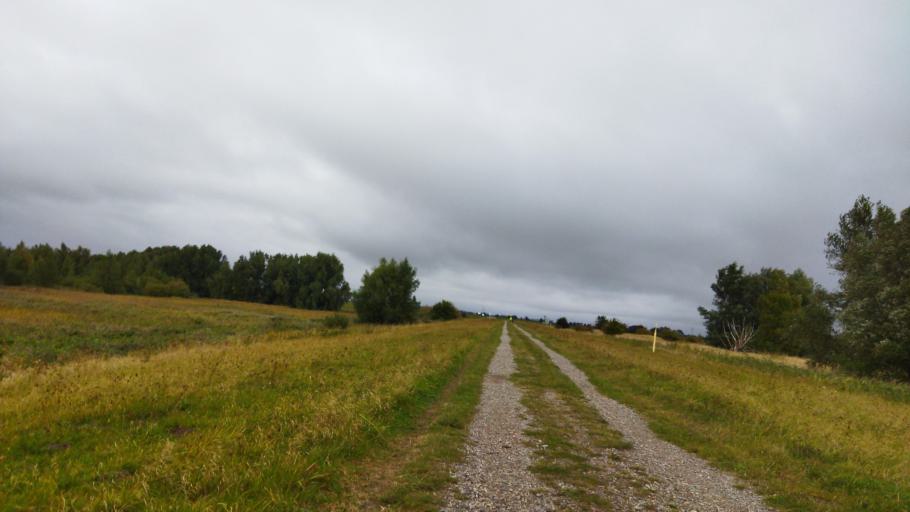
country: NL
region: Groningen
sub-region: Gemeente Delfzijl
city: Delfzijl
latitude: 53.3763
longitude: 7.0127
